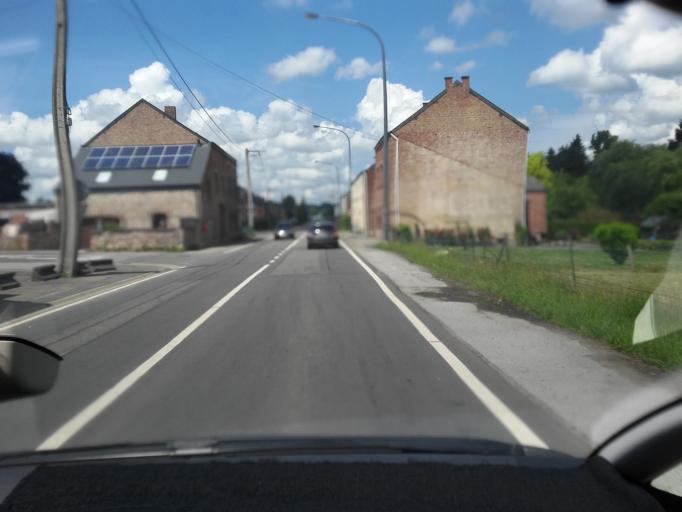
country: BE
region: Wallonia
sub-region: Province de Namur
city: Rochefort
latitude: 50.1695
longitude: 5.2115
